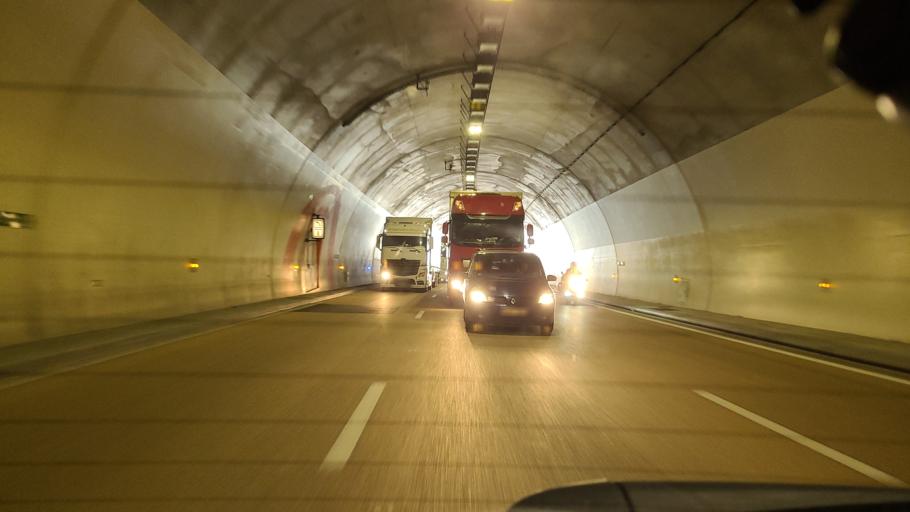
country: FR
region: Provence-Alpes-Cote d'Azur
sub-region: Departement des Alpes-Maritimes
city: Eze
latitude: 43.7434
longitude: 7.3534
